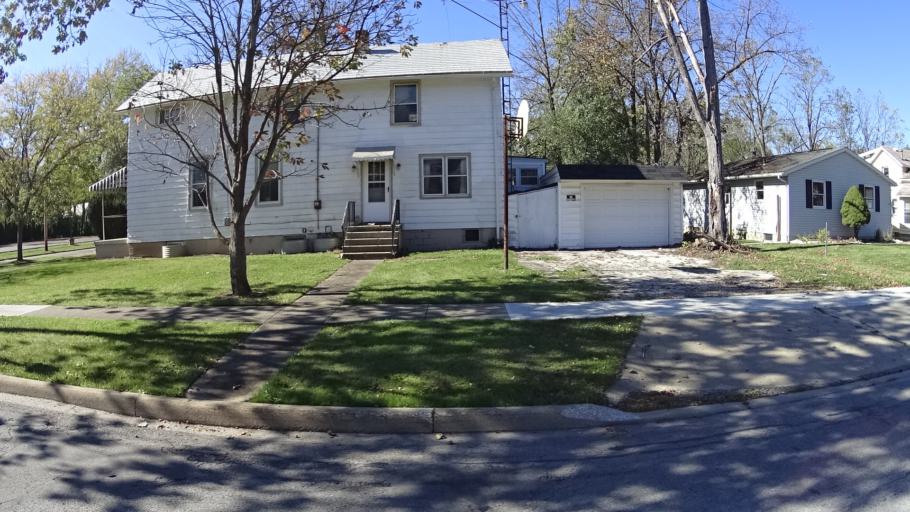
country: US
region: Ohio
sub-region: Lorain County
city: Oberlin
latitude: 41.2864
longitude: -82.2150
